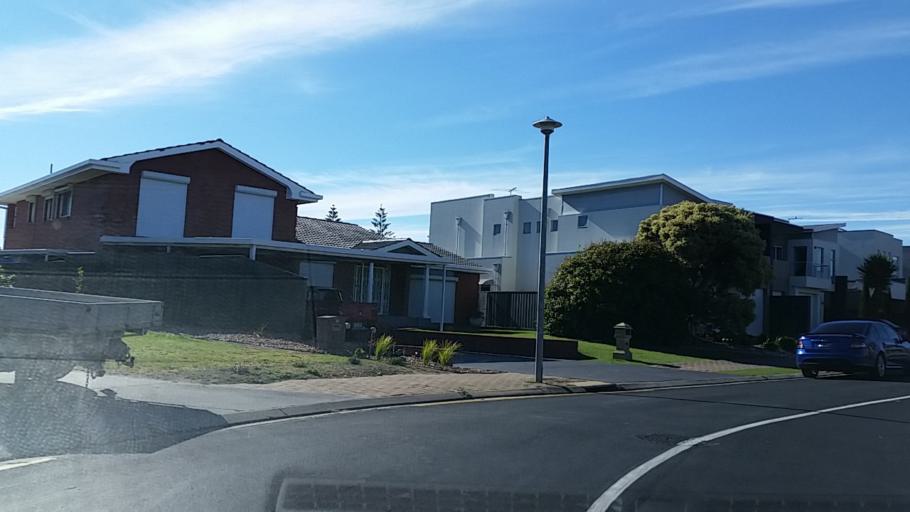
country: AU
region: South Australia
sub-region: Charles Sturt
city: West Lakes Shore
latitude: -34.8711
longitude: 138.4867
